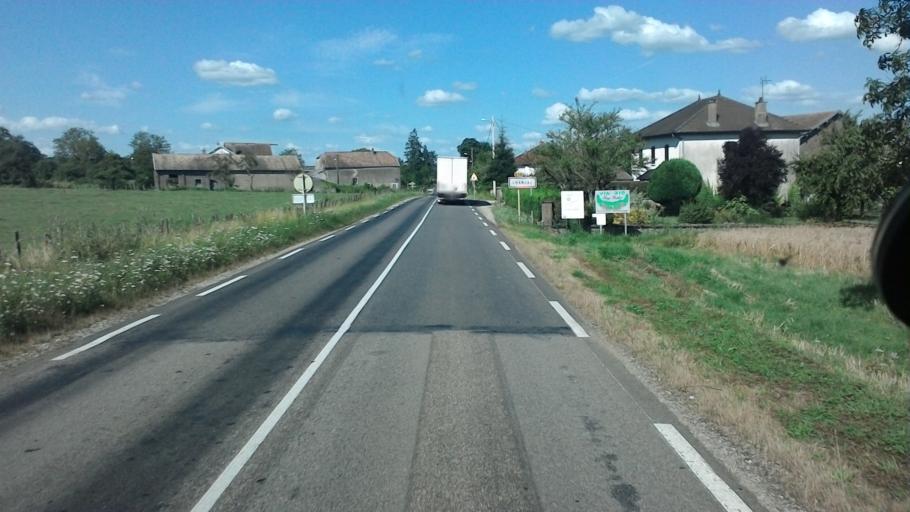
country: FR
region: Franche-Comte
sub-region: Departement de la Haute-Saone
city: Marnay
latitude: 47.3194
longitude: 5.6775
